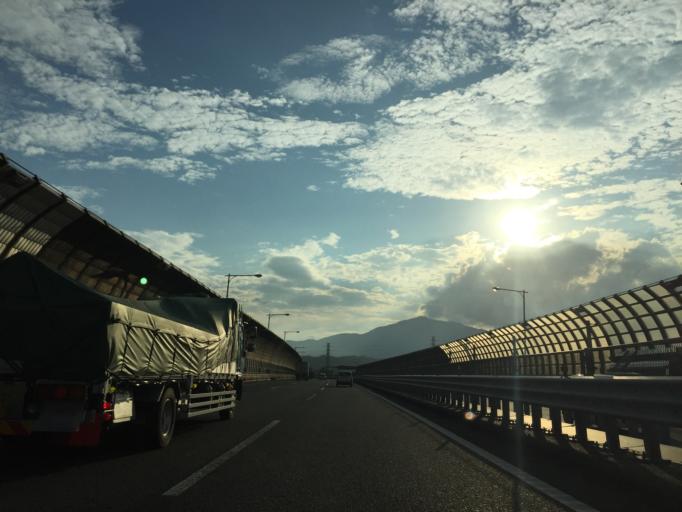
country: JP
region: Kanagawa
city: Atsugi
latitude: 35.4250
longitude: 139.3517
